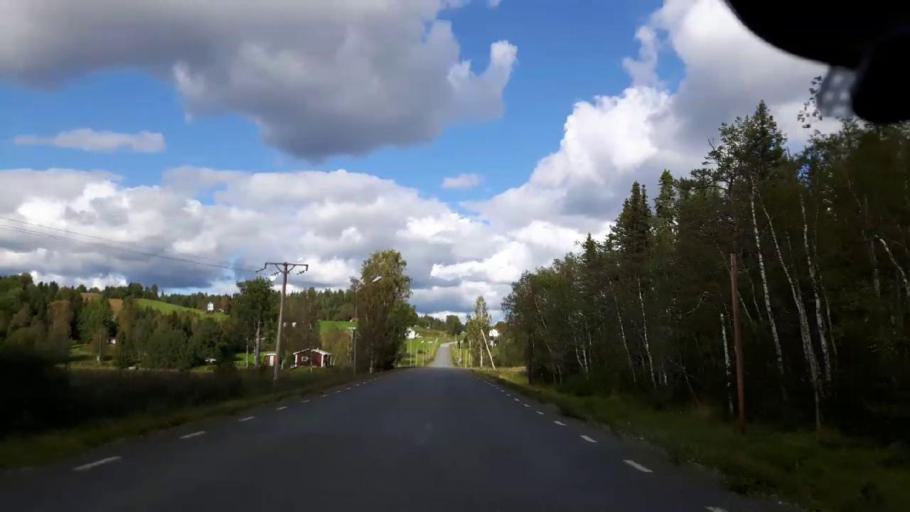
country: SE
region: Jaemtland
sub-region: Stroemsunds Kommun
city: Stroemsund
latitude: 63.2936
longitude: 15.5931
